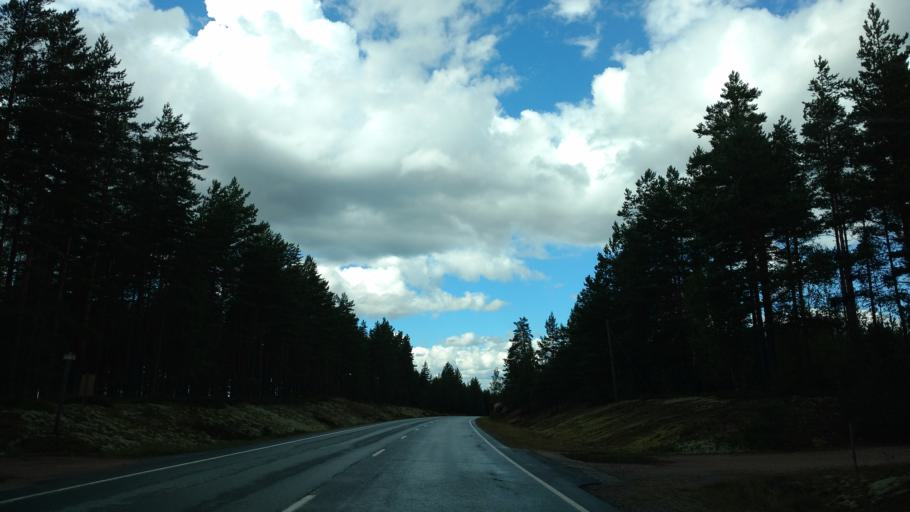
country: FI
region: Varsinais-Suomi
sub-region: Salo
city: Muurla
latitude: 60.2955
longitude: 23.3320
